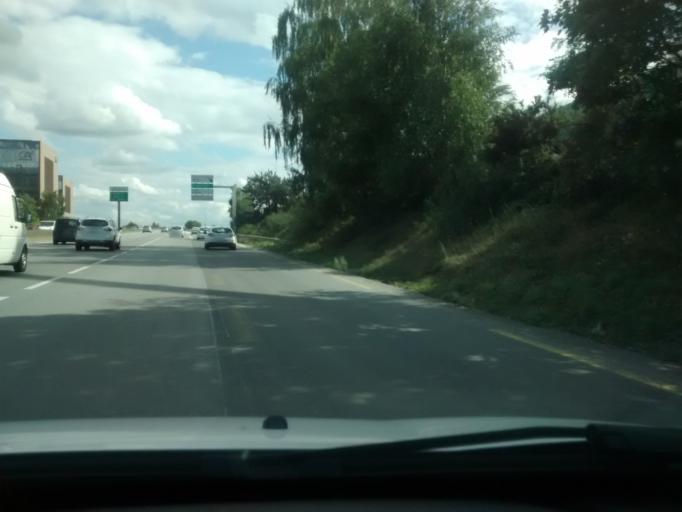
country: FR
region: Brittany
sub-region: Departement d'Ille-et-Vilaine
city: Saint-Jacques-de-la-Lande
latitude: 48.0937
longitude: -1.7095
